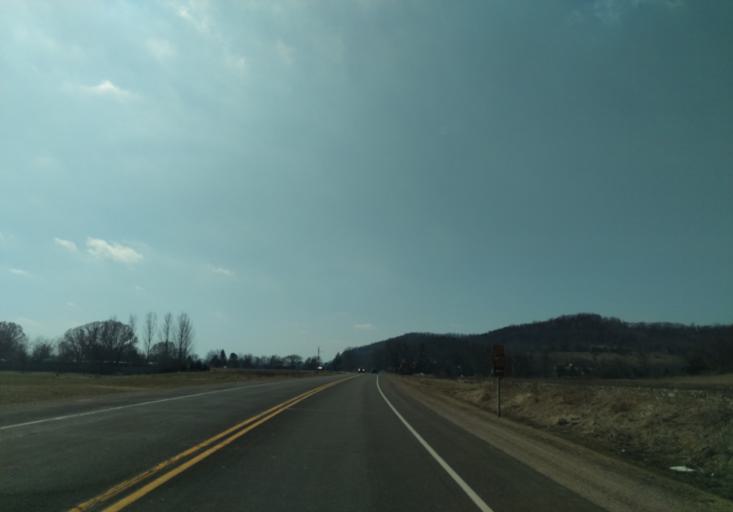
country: US
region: Wisconsin
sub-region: La Crosse County
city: La Crosse
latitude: 43.7619
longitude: -91.1825
